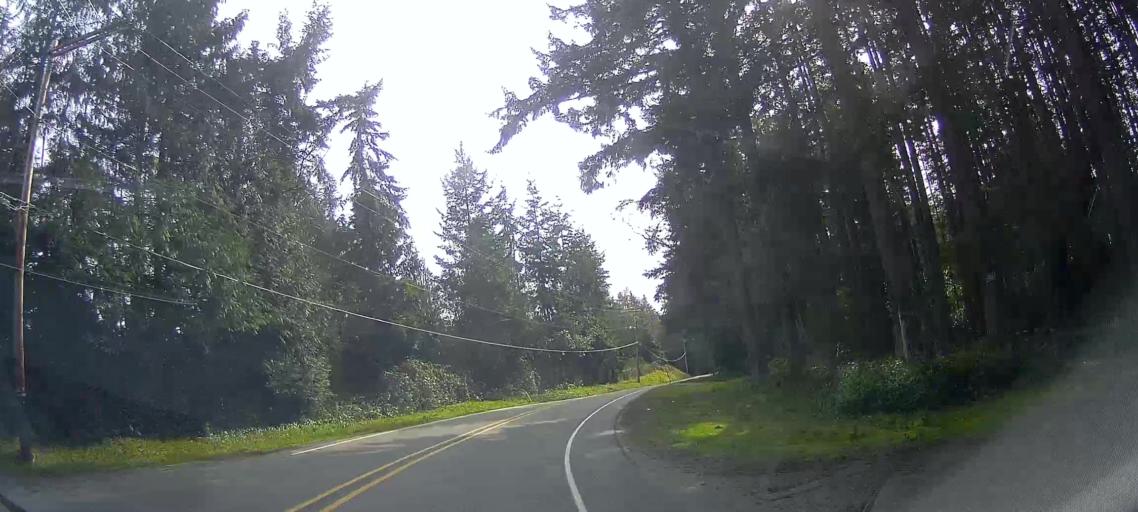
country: US
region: Washington
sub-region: Island County
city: Langley
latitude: 48.1205
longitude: -122.4509
